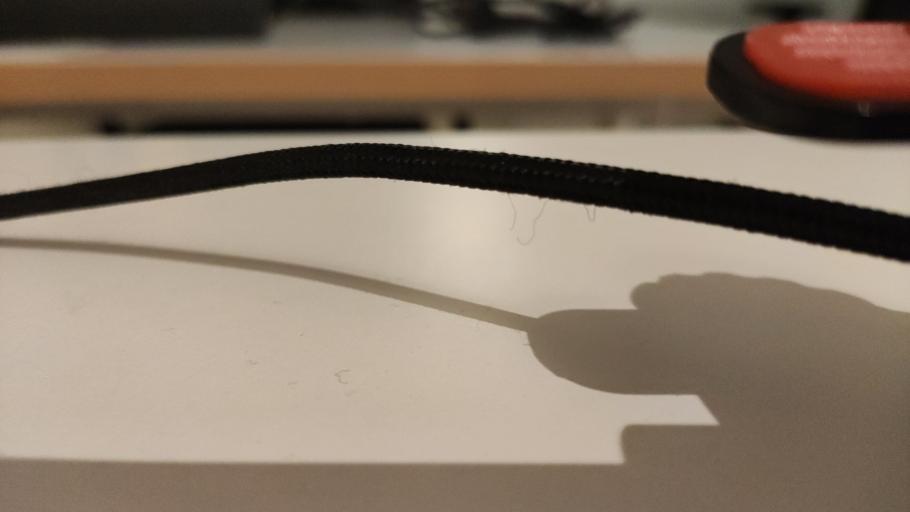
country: RU
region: Moskovskaya
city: Novoye
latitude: 55.6601
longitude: 38.9396
